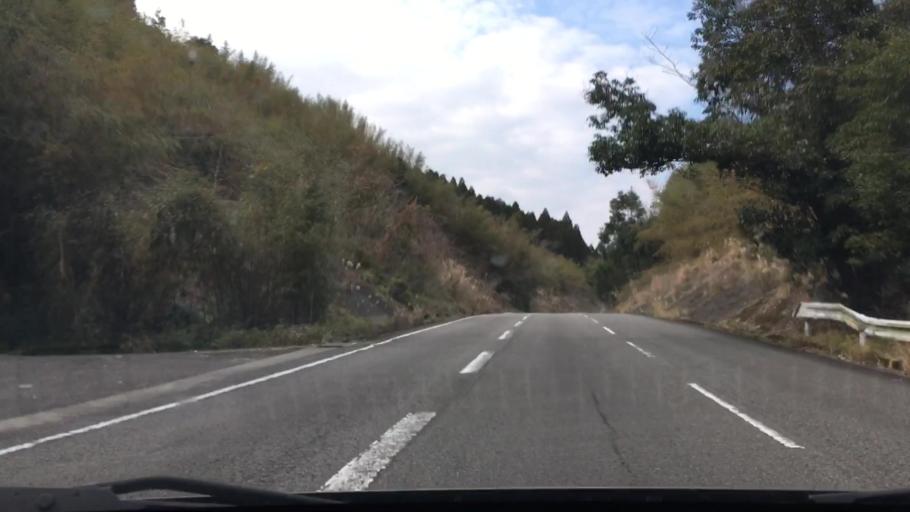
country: JP
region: Miyazaki
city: Nichinan
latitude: 31.6350
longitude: 131.3378
